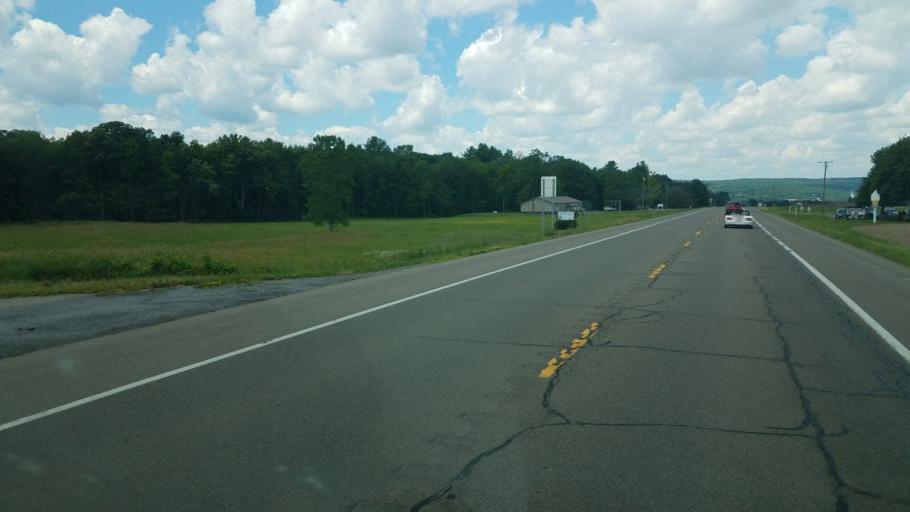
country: US
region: New York
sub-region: Yates County
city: Penn Yan
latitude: 42.6379
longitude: -77.0425
